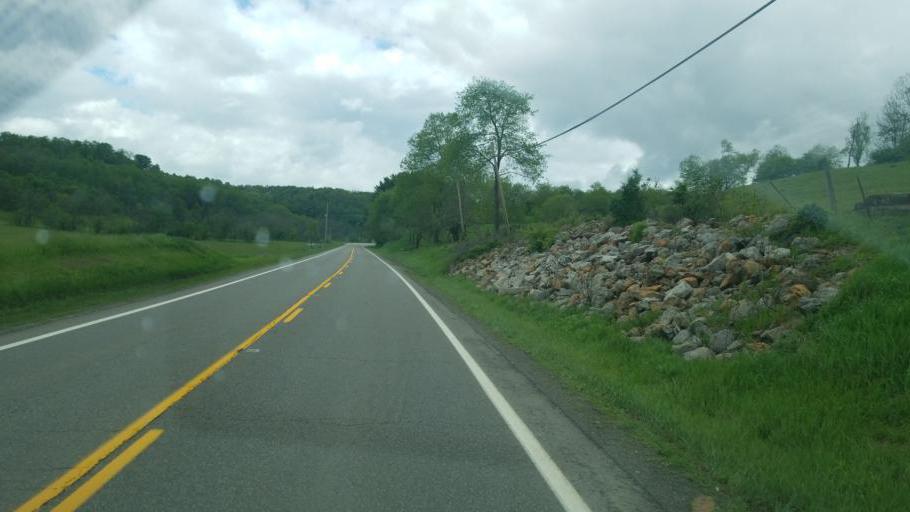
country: US
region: Ohio
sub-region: Harrison County
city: Cadiz
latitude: 40.2941
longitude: -81.0636
